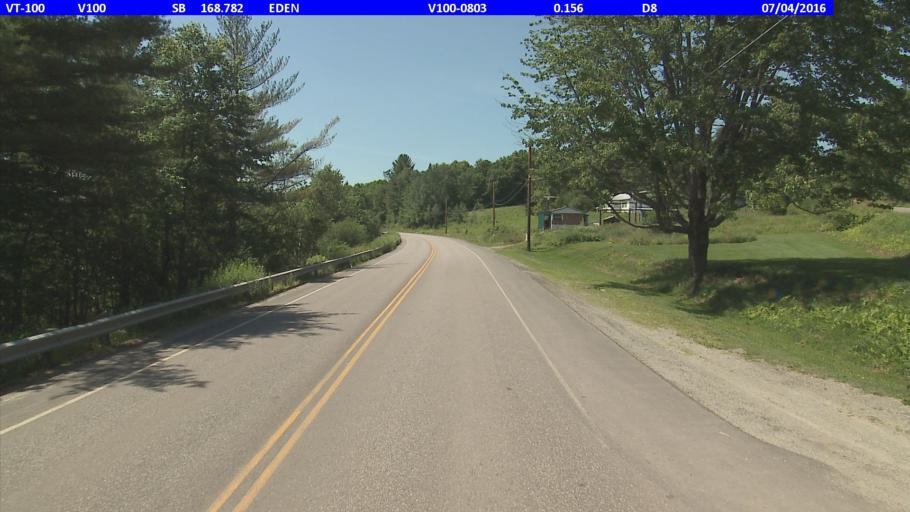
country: US
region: Vermont
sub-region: Lamoille County
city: Hyde Park
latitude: 44.6859
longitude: -72.5897
